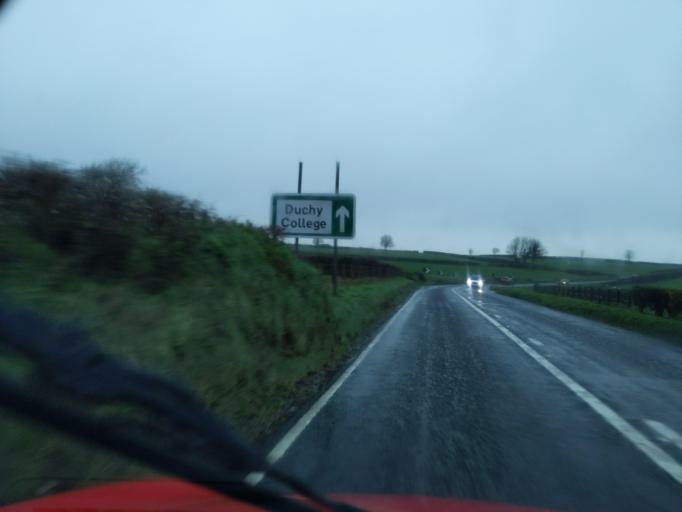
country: GB
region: England
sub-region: Cornwall
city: South Hill
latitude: 50.5435
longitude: -4.3365
